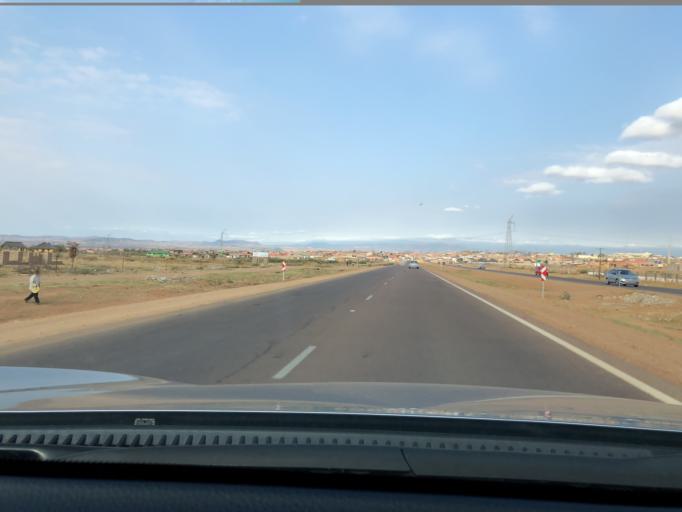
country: ZA
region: Limpopo
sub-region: Capricorn District Municipality
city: Mankoeng
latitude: -23.8873
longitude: 29.6813
